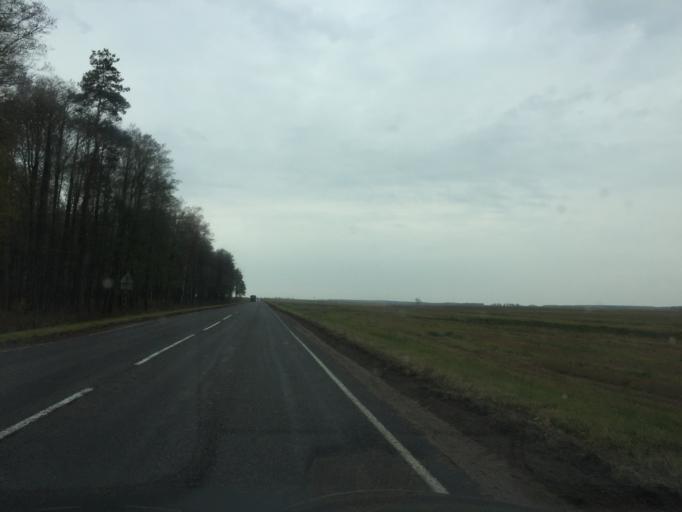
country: BY
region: Gomel
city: Dowsk
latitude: 53.1900
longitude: 30.5065
